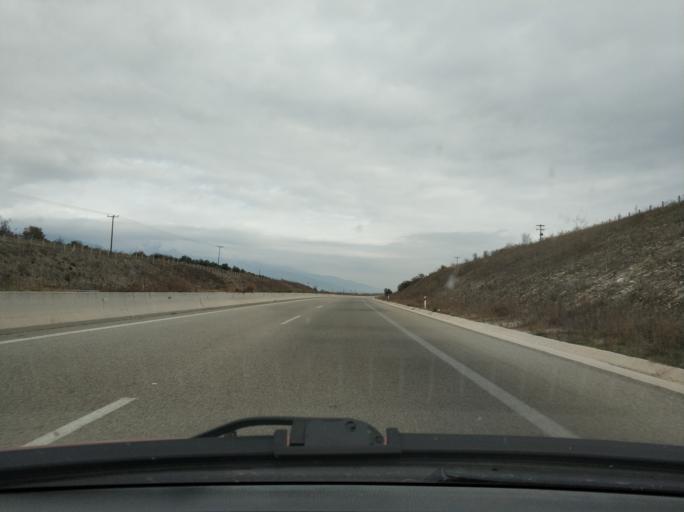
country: GR
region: Central Macedonia
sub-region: Nomos Serron
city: Rodolivos
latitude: 40.8030
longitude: 24.0228
